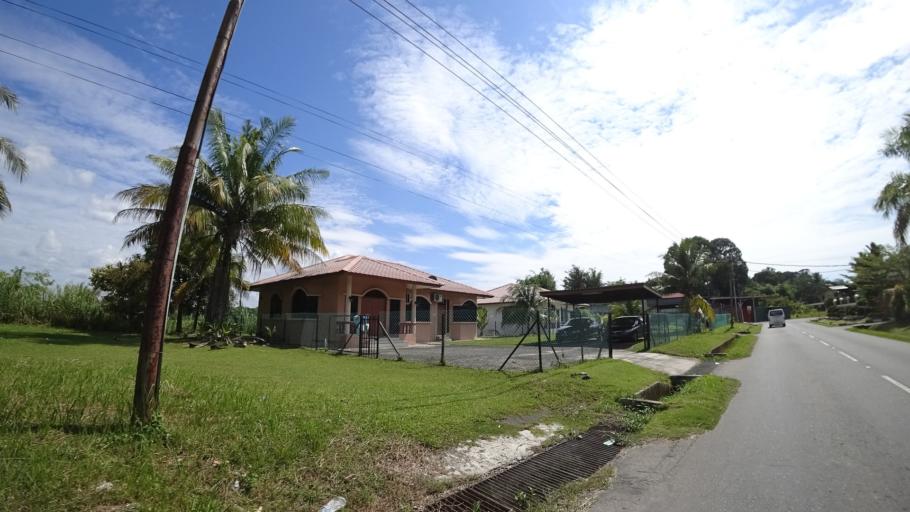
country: BN
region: Brunei and Muara
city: Bandar Seri Begawan
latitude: 4.8969
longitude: 114.8437
